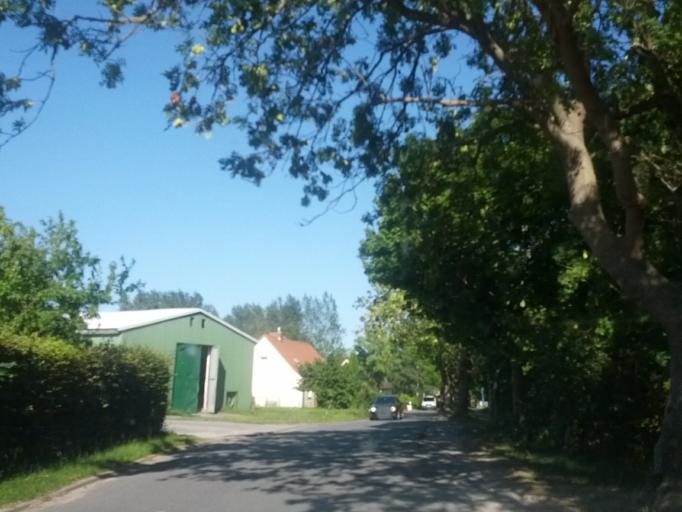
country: DE
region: Mecklenburg-Vorpommern
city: Ostseebad Gohren
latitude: 54.3311
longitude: 13.7015
